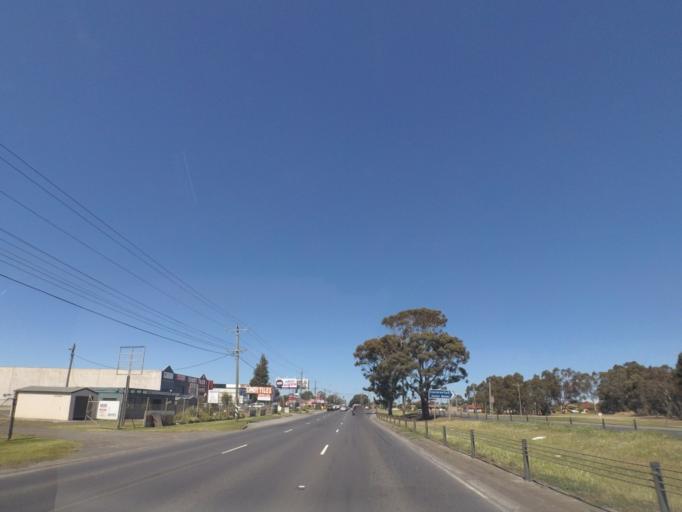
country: AU
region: Victoria
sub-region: Hume
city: Campbellfield
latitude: -37.6651
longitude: 144.9548
